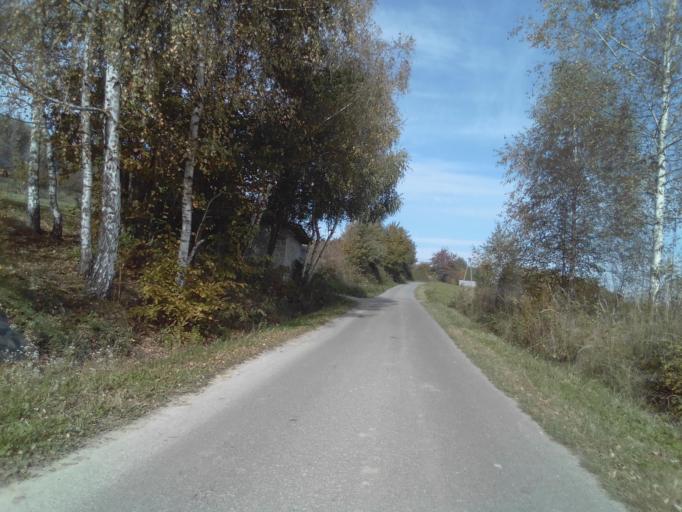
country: PL
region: Subcarpathian Voivodeship
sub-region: Powiat strzyzowski
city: Gwoznica Gorna
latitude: 49.8469
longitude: 21.9655
